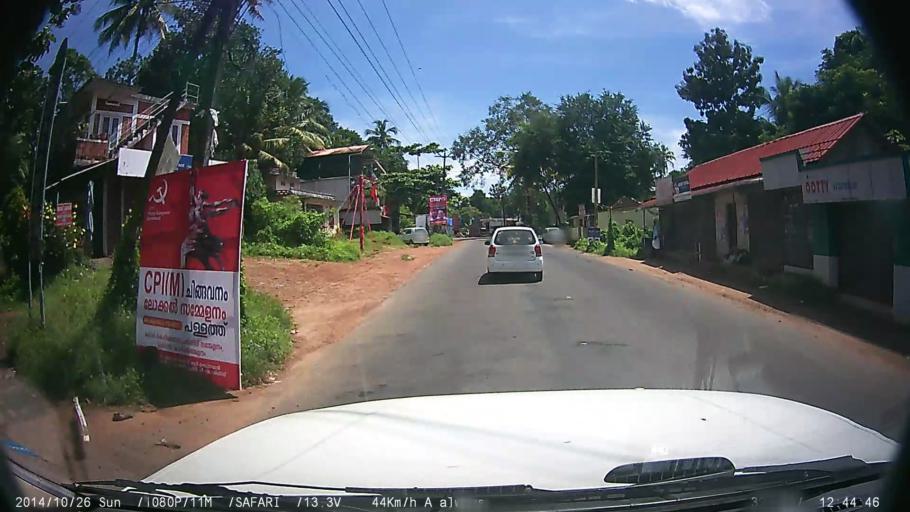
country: IN
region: Kerala
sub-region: Kottayam
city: Kottayam
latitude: 9.5290
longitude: 76.5146
